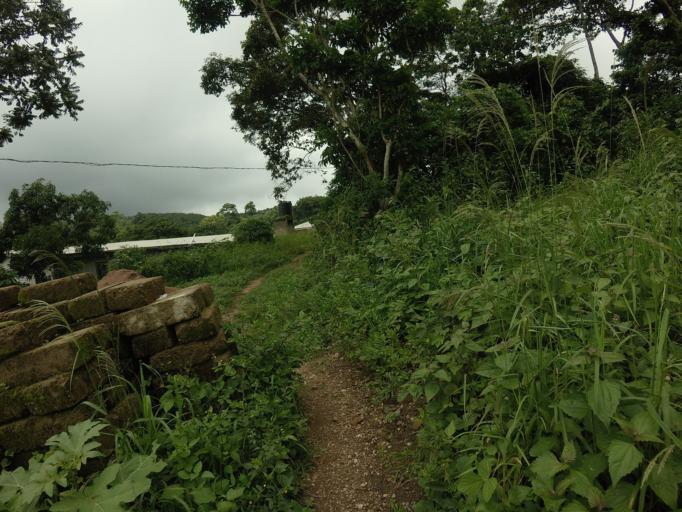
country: TG
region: Plateaux
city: Kpalime
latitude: 6.8449
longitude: 0.4416
